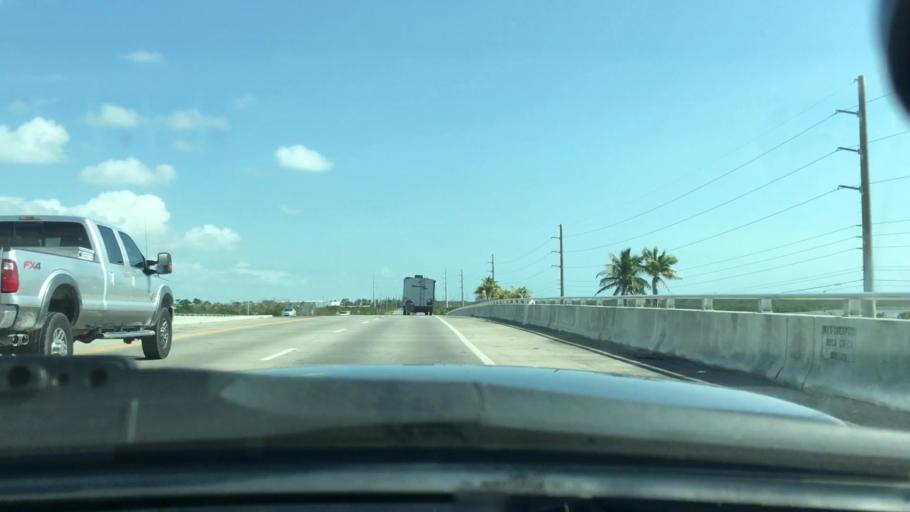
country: US
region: Florida
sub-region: Monroe County
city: Big Coppitt Key
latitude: 24.5881
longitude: -81.6910
